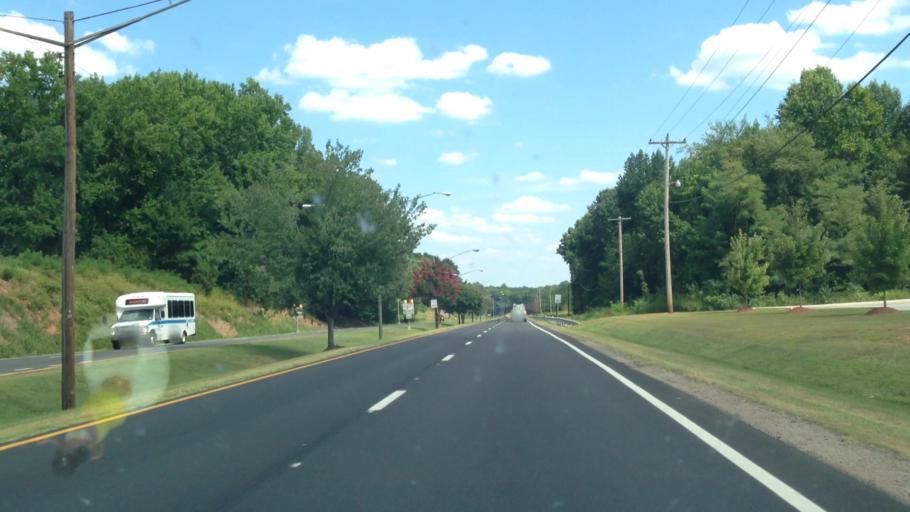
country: US
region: Virginia
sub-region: City of Danville
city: Danville
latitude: 36.5860
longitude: -79.4488
